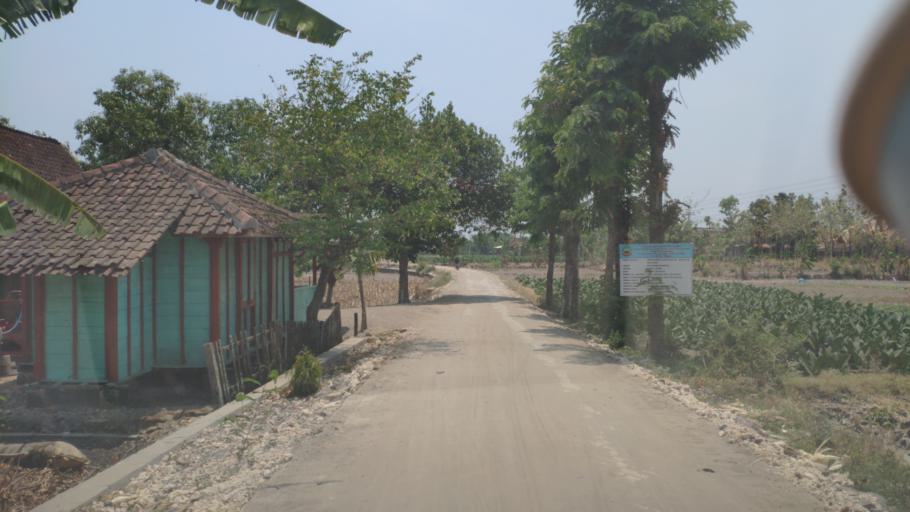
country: ID
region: Central Java
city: Temulus
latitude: -7.2310
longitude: 111.4226
